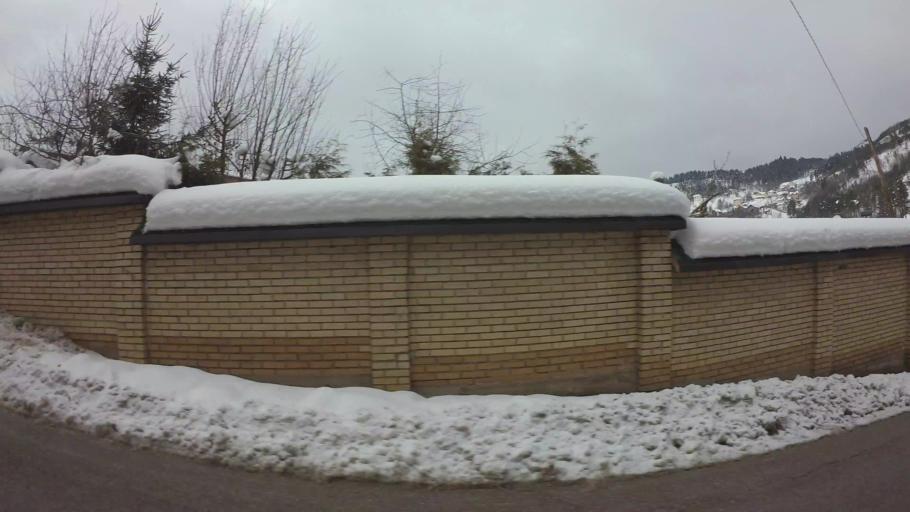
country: BA
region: Federation of Bosnia and Herzegovina
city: Kobilja Glava
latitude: 43.8730
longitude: 18.4414
